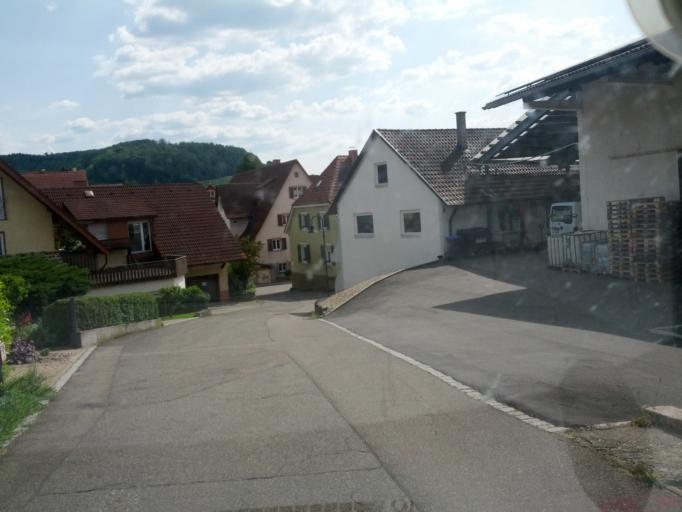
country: DE
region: Baden-Wuerttemberg
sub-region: Freiburg Region
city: Ebringen
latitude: 47.9586
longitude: 7.7767
